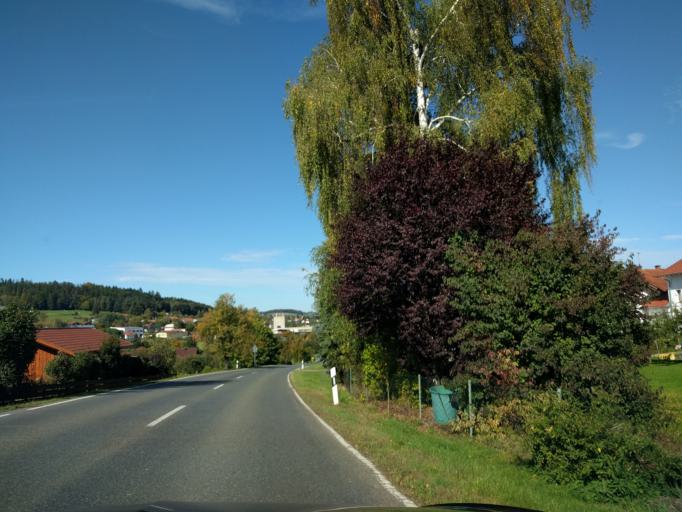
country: DE
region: Bavaria
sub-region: Upper Palatinate
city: Kotzting
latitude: 49.1641
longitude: 12.8774
